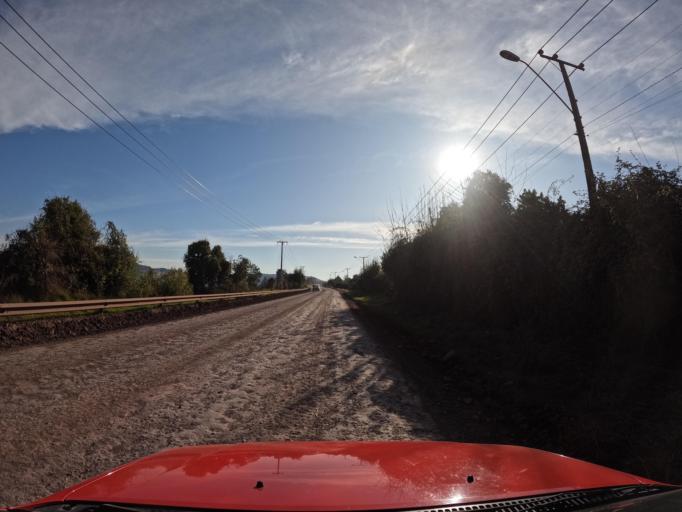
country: CL
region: Maule
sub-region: Provincia de Curico
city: Teno
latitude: -34.9619
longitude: -70.9620
